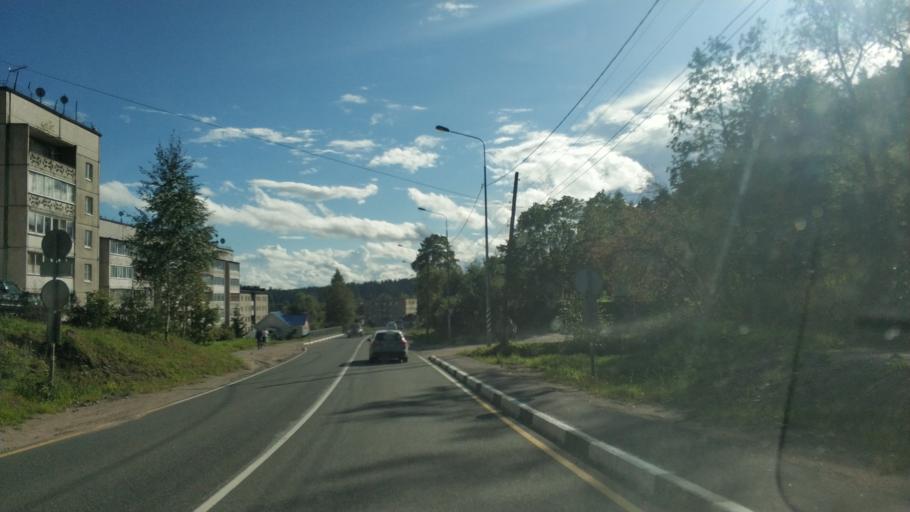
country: RU
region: Republic of Karelia
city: Lakhdenpokh'ya
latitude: 61.5242
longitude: 30.1999
